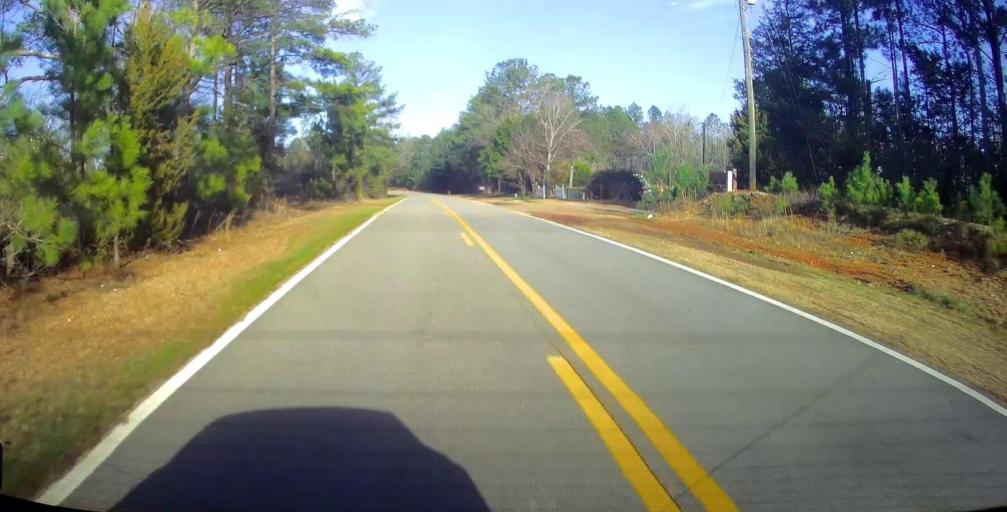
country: US
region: Georgia
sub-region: Crawford County
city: Knoxville
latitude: 32.8263
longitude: -83.9419
